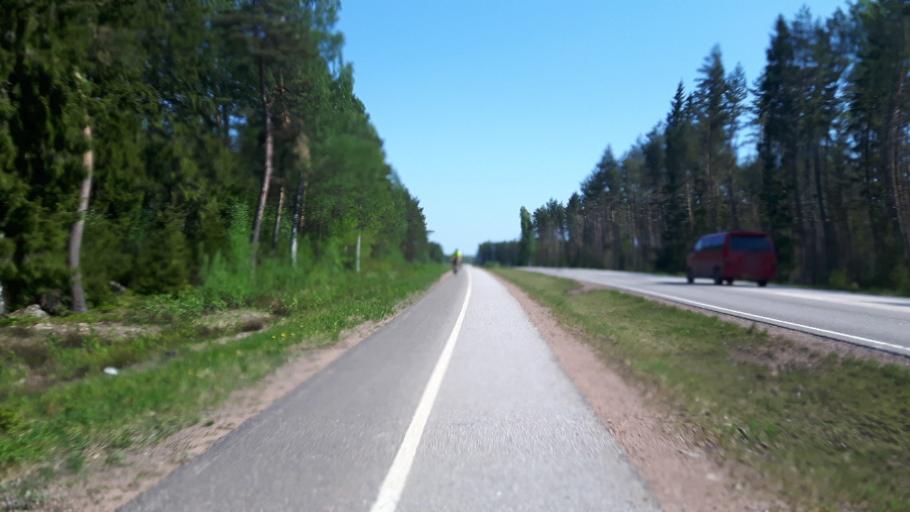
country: FI
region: Kymenlaakso
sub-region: Kotka-Hamina
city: Pyhtaeae
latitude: 60.4889
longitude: 26.5063
